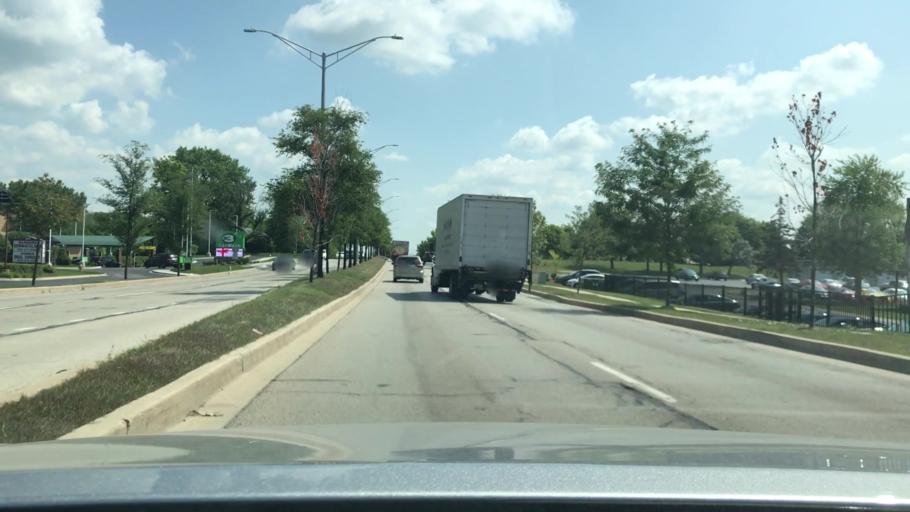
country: US
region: Illinois
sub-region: DuPage County
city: Woodridge
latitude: 41.7194
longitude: -88.0469
